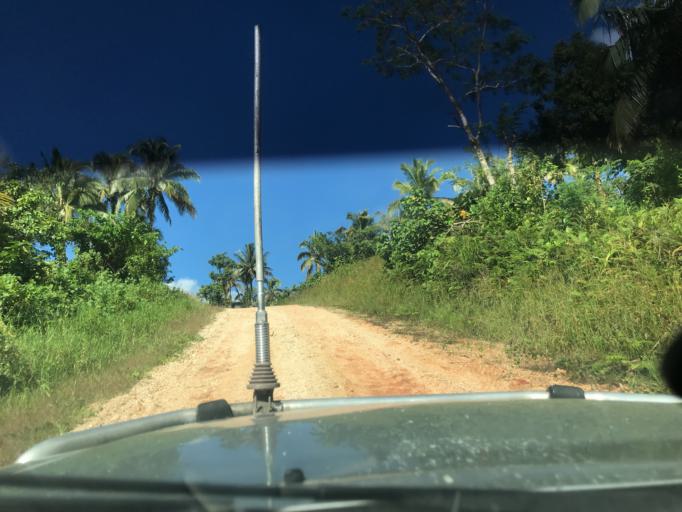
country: SB
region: Malaita
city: Auki
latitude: -8.6192
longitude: 160.7409
